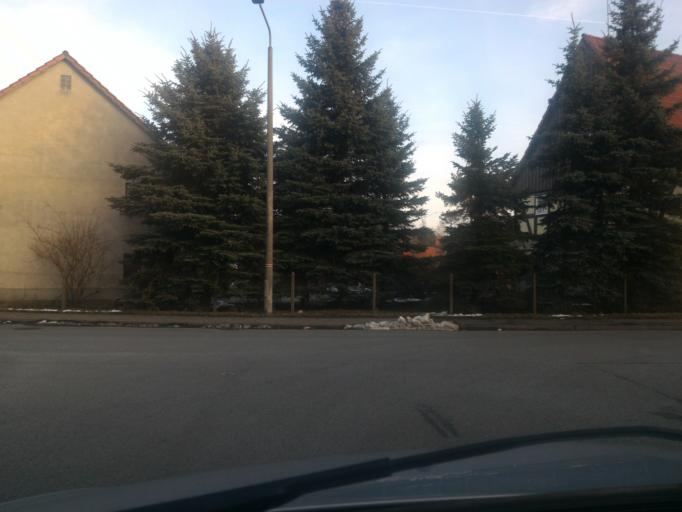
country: DE
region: Saxony
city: Olbersdorf
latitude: 50.8713
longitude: 14.7665
